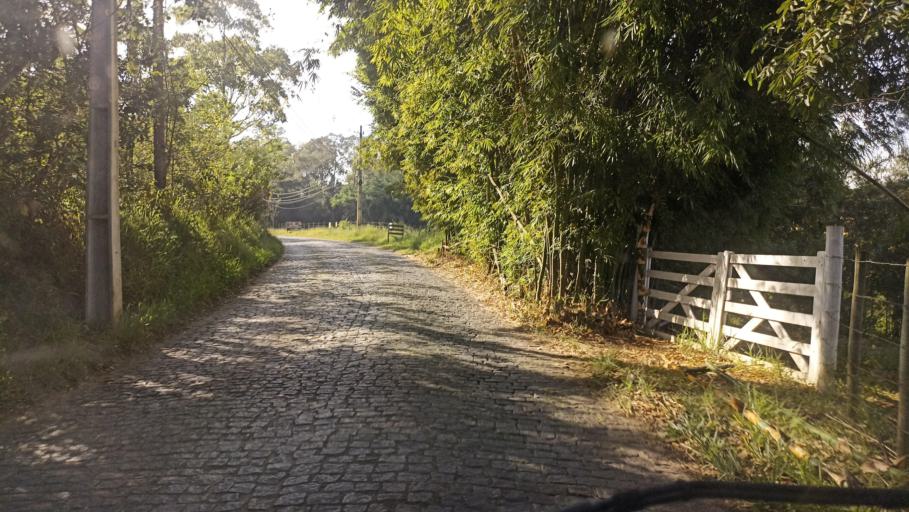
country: BR
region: Minas Gerais
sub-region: Tiradentes
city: Tiradentes
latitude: -21.1204
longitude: -44.1927
